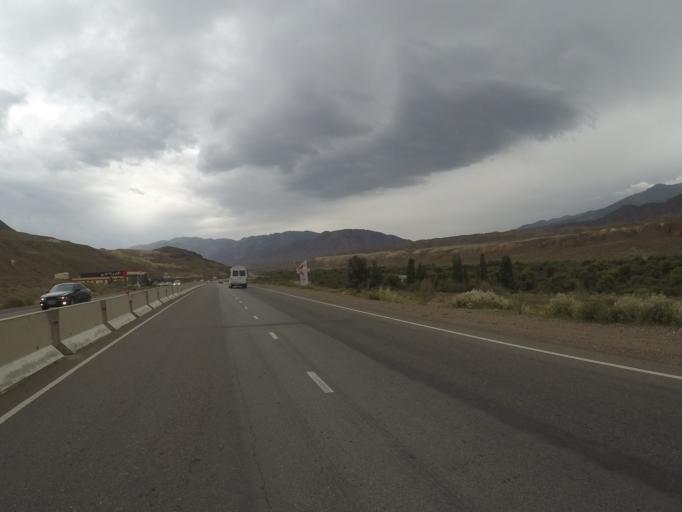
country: KG
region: Naryn
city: Kochkor
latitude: 42.5080
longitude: 75.8339
